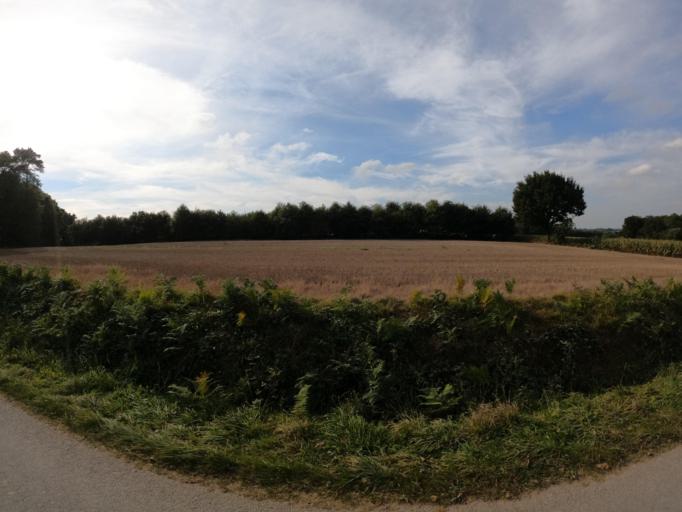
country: FR
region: Brittany
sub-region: Departement du Morbihan
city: Caro
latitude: 47.8832
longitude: -2.3499
